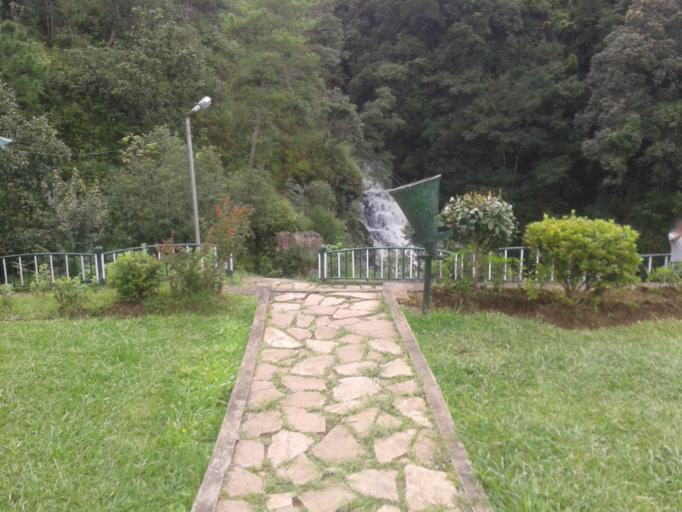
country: IN
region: Meghalaya
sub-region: East Khasi Hills
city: Shillong
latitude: 25.5384
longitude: 91.8220
